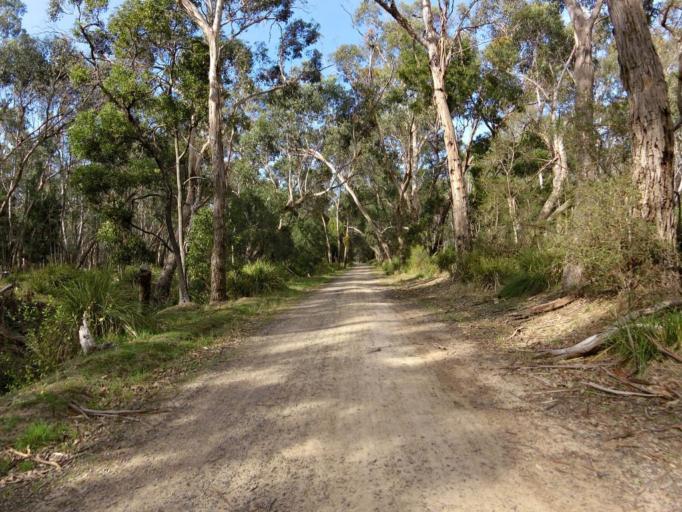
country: AU
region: Victoria
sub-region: Yarra Ranges
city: Lysterfield
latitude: -37.9488
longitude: 145.2903
